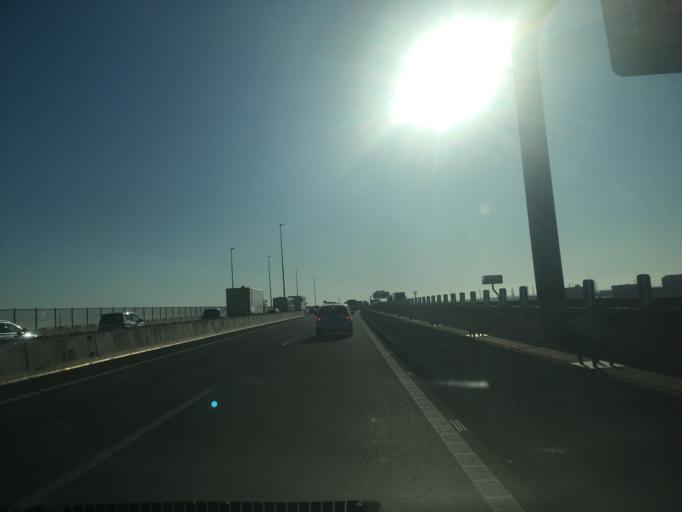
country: JP
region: Saitama
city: Kukichuo
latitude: 36.0474
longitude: 139.6656
